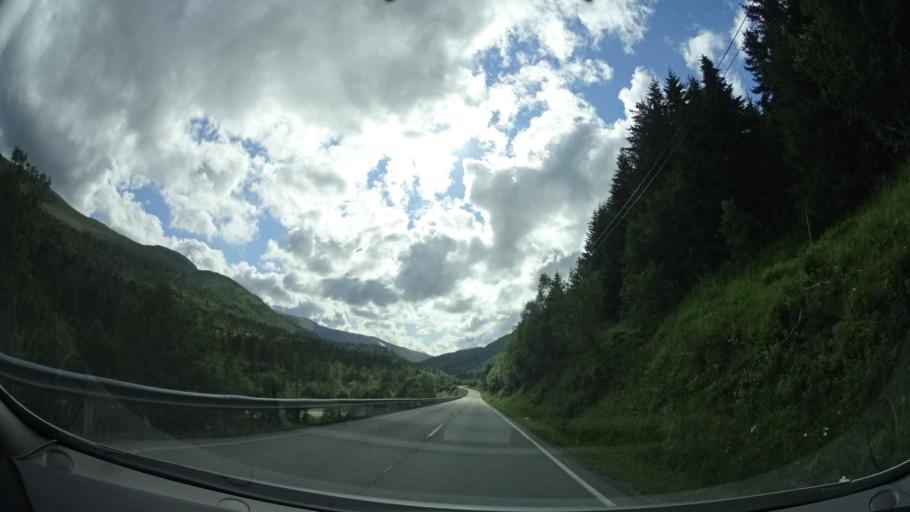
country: NO
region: Sor-Trondelag
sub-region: Hemne
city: Kyrksaeterora
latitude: 63.2198
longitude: 9.2205
